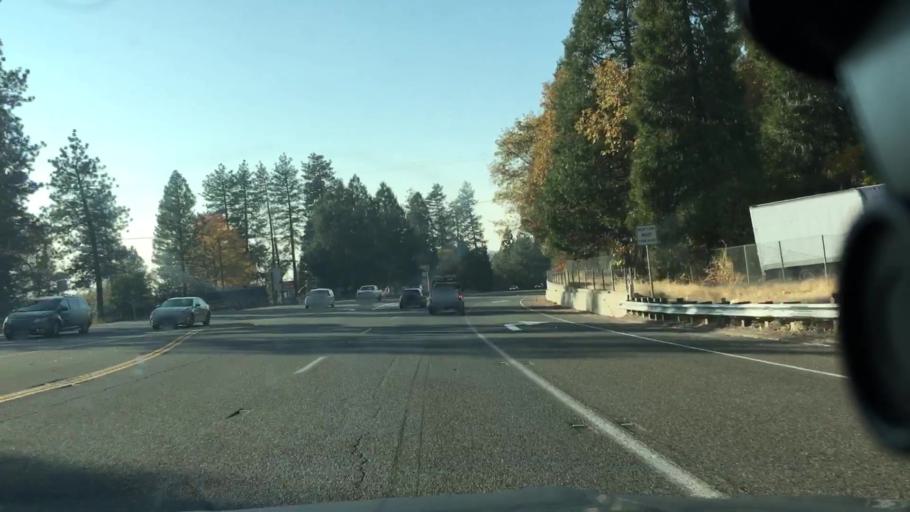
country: US
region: California
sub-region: El Dorado County
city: Camino
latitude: 38.7371
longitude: -120.7158
